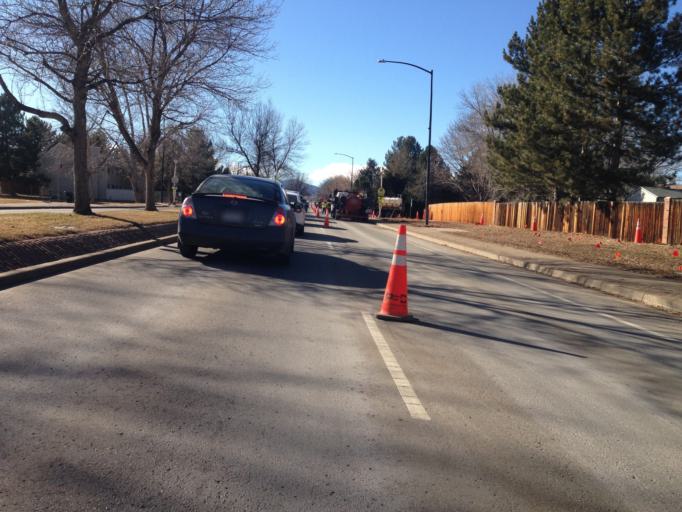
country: US
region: Colorado
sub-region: Boulder County
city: Louisville
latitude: 39.9871
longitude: -105.1127
